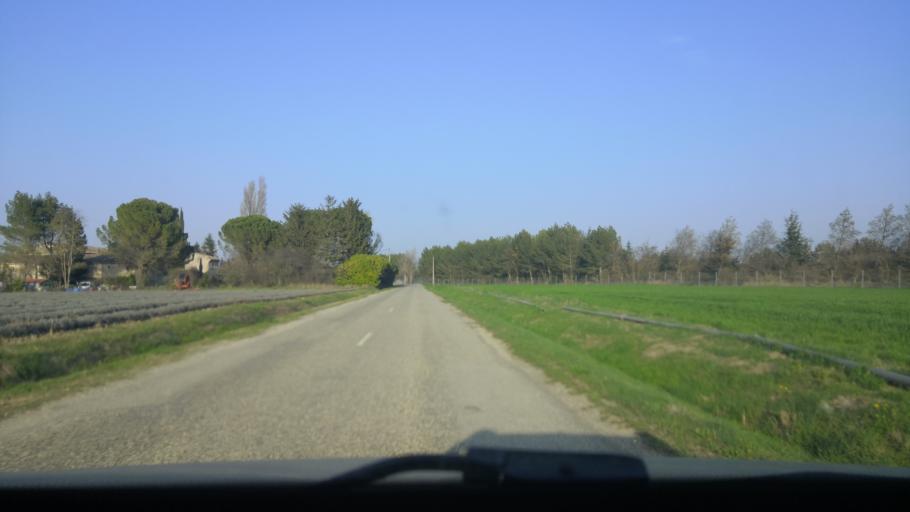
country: FR
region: Rhone-Alpes
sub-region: Departement de la Drome
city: Montboucher-sur-Jabron
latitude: 44.5497
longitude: 4.8251
